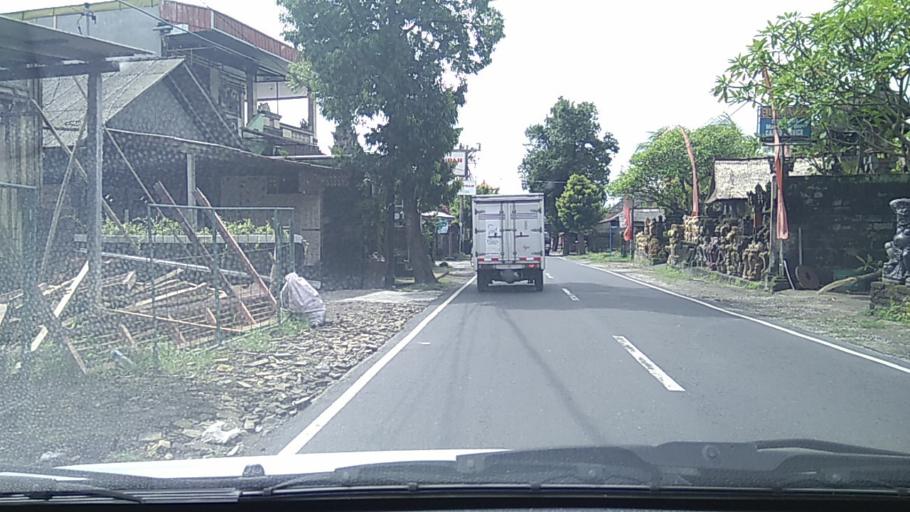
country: ID
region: Bali
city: Banjar Sedang
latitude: -8.5731
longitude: 115.2569
